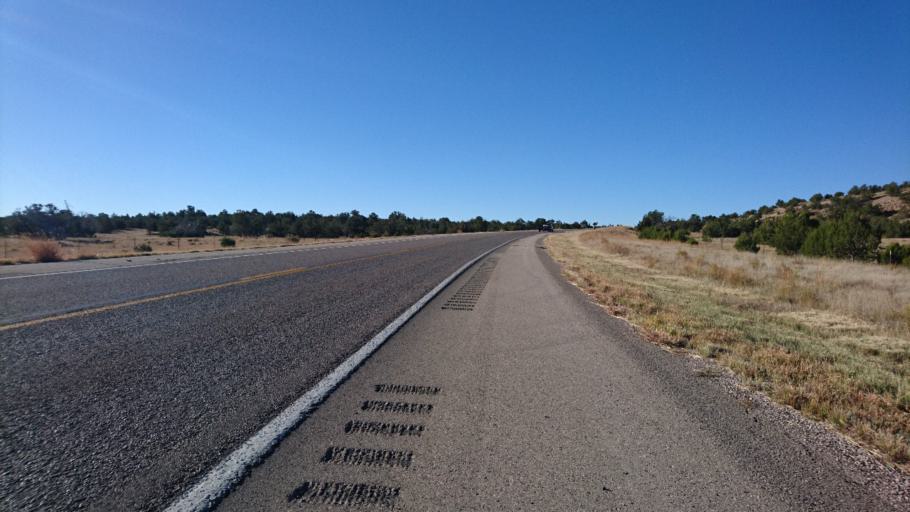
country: US
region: New Mexico
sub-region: Cibola County
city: Grants
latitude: 34.9661
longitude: -107.9130
